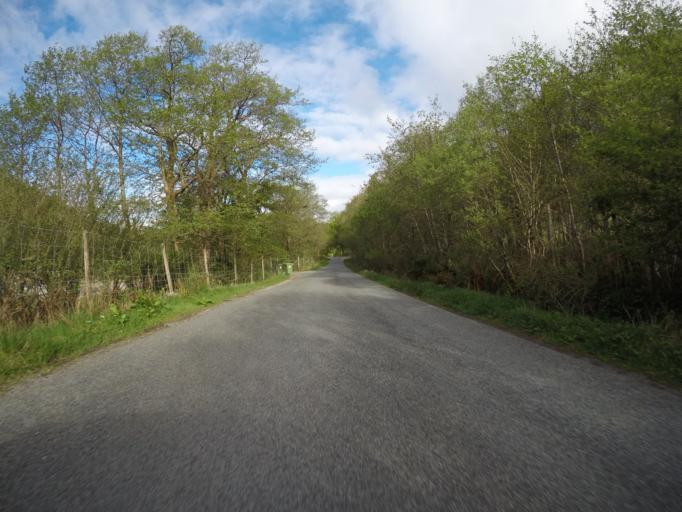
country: GB
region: Scotland
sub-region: Highland
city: Fort William
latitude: 56.6802
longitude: -5.0846
